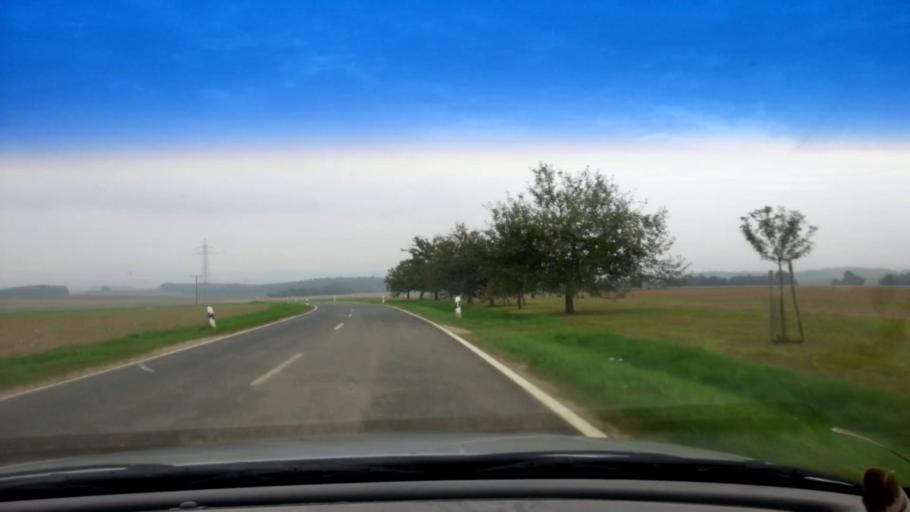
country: DE
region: Bavaria
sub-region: Upper Franconia
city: Ebensfeld
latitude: 50.0669
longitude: 10.9102
